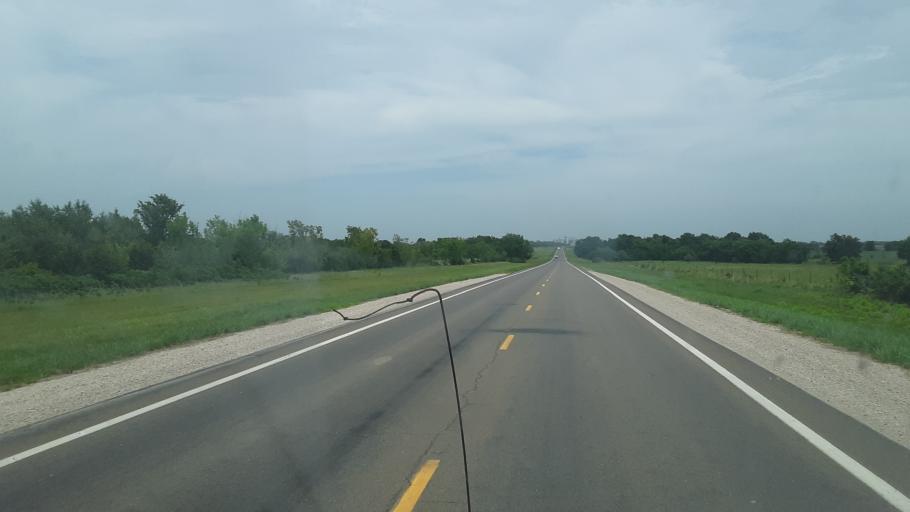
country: US
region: Kansas
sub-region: Woodson County
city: Yates Center
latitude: 37.9141
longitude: -95.5711
